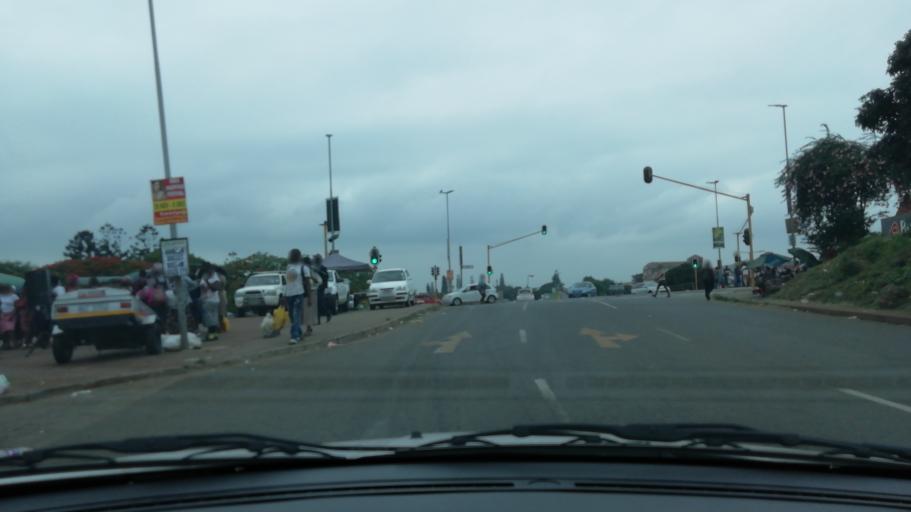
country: ZA
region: KwaZulu-Natal
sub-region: uThungulu District Municipality
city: Empangeni
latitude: -28.7446
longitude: 31.8851
